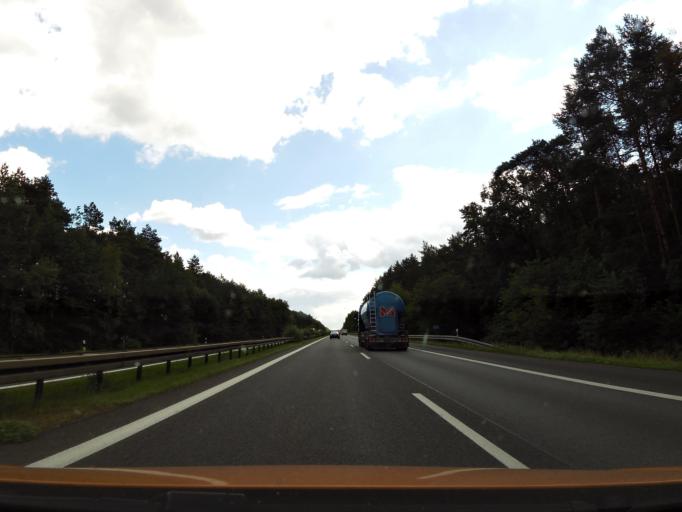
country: DE
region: Brandenburg
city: Birkenwerder
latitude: 52.6954
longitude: 13.3025
